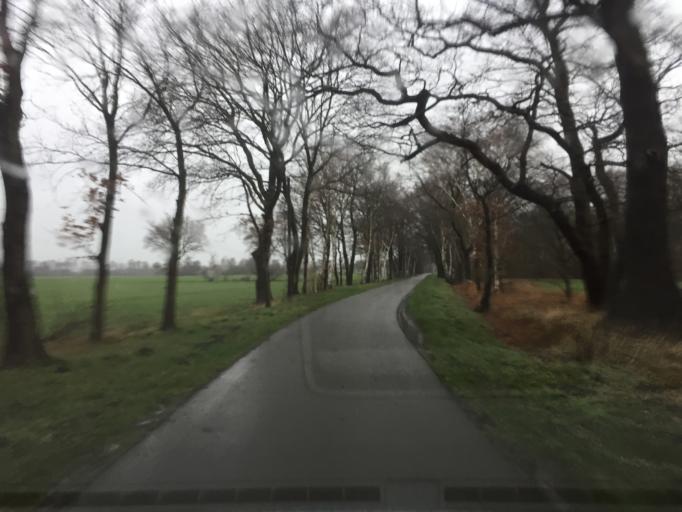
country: DE
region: Lower Saxony
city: Borstel
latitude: 52.6335
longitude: 8.9267
